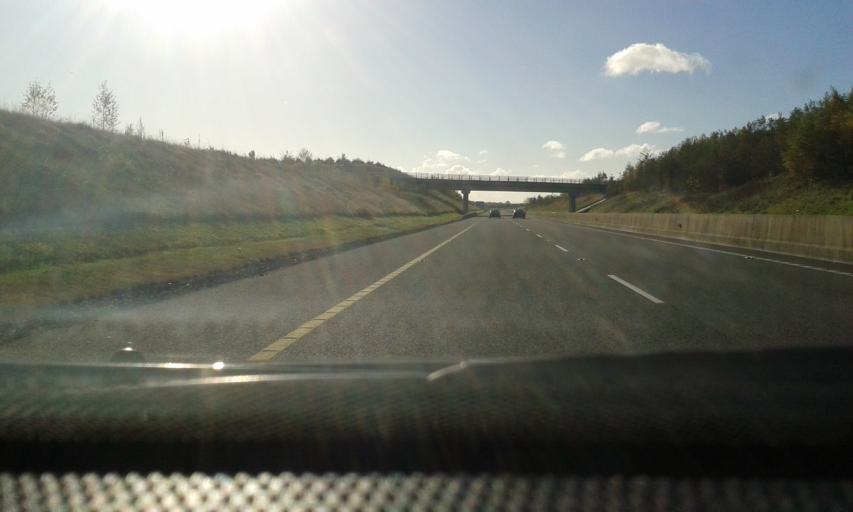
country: IE
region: Leinster
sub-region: Laois
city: Rathdowney
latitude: 52.8953
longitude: -7.4906
